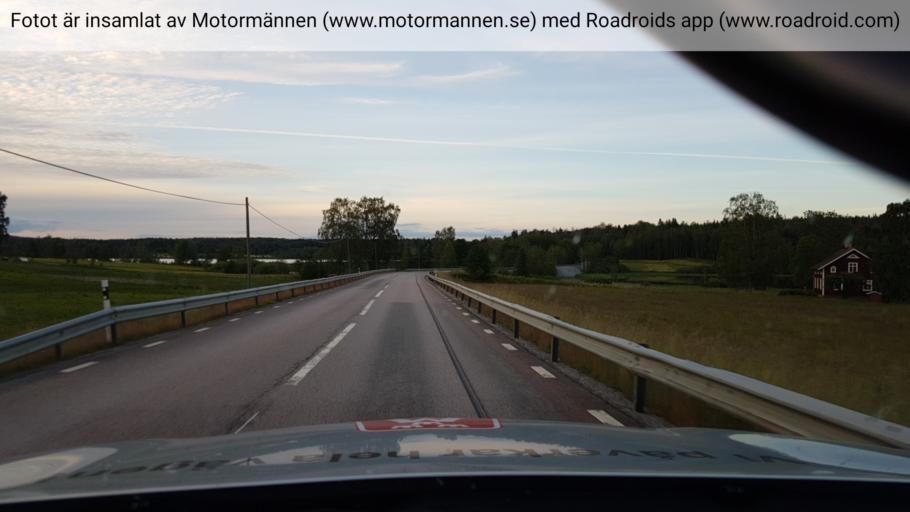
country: SE
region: Vaestmanland
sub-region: Skinnskattebergs Kommun
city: Skinnskatteberg
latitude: 59.8779
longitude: 15.6597
